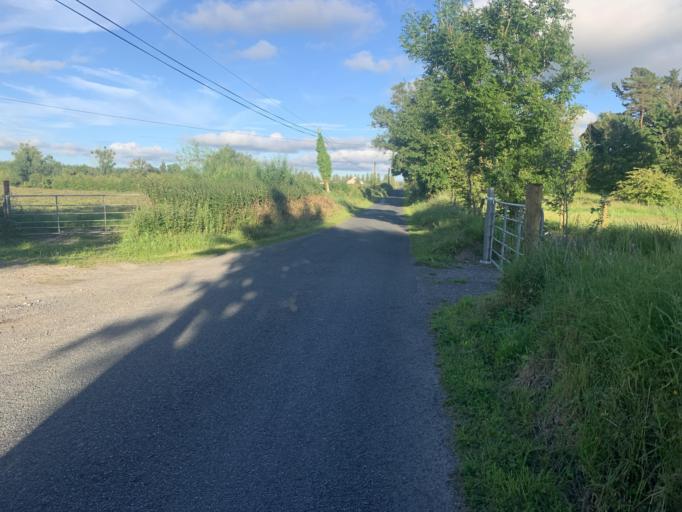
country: IE
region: Connaught
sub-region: Sligo
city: Tobercurry
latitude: 54.0165
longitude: -8.7565
